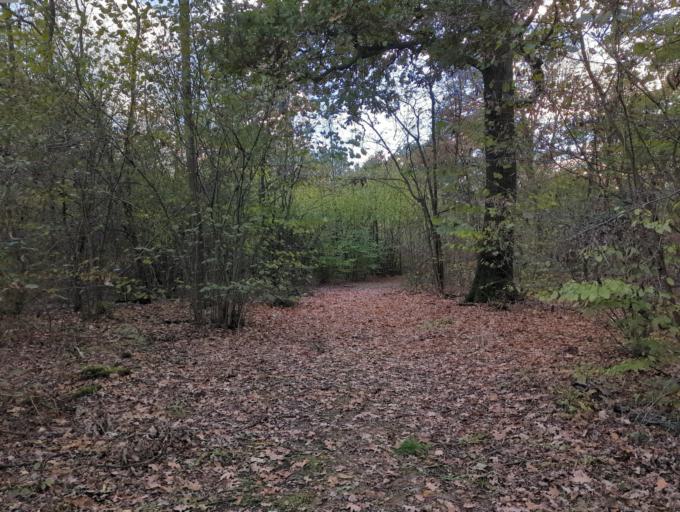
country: IT
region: Piedmont
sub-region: Provincia di Vercelli
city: Palazzolo Vercellese
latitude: 45.2133
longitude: 8.2605
